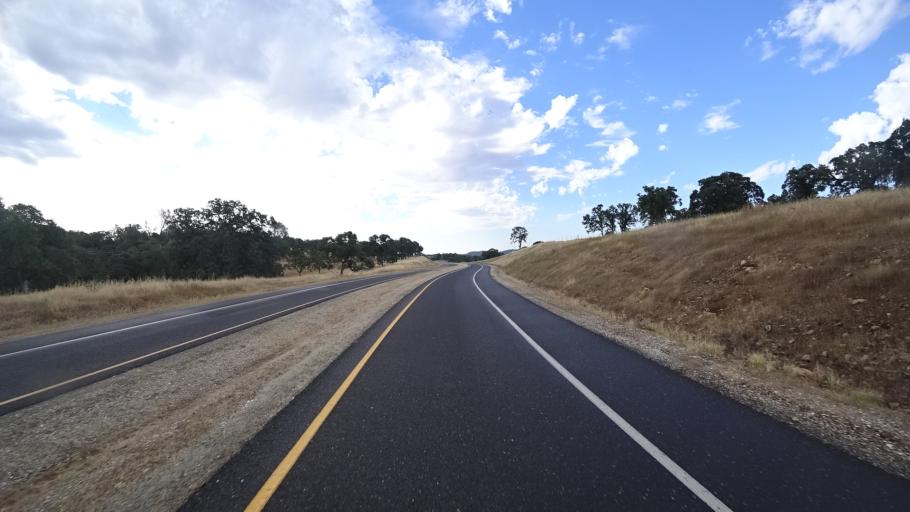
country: US
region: California
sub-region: Calaveras County
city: Copperopolis
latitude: 37.9425
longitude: -120.6480
